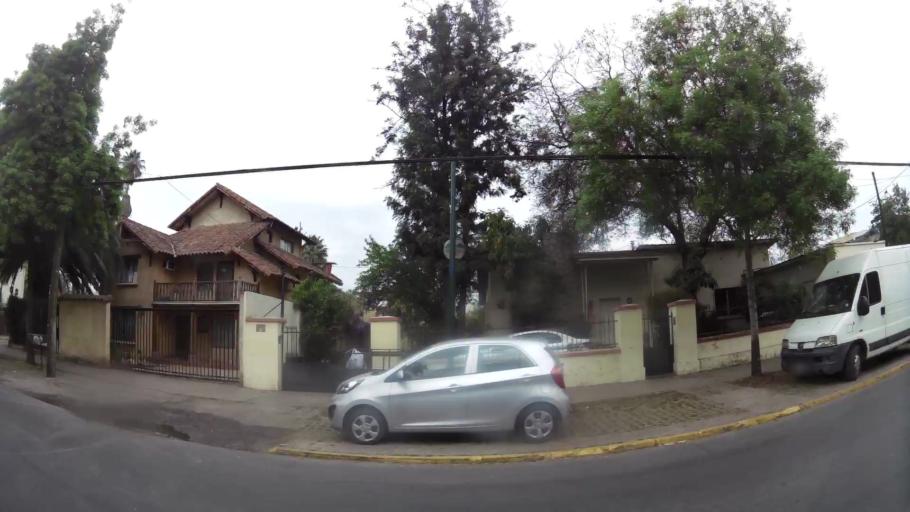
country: CL
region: Santiago Metropolitan
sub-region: Provincia de Santiago
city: Villa Presidente Frei, Nunoa, Santiago, Chile
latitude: -33.4634
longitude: -70.5942
